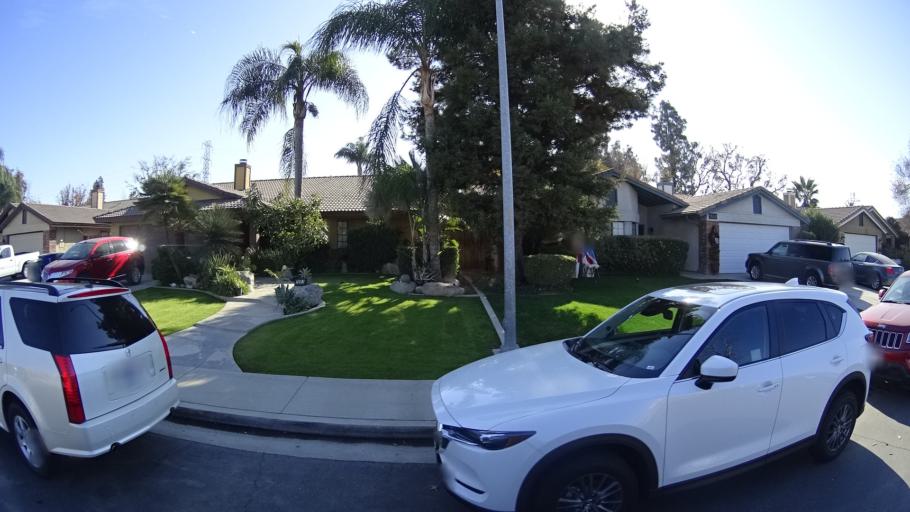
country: US
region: California
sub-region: Kern County
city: Greenacres
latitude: 35.3991
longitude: -119.0869
